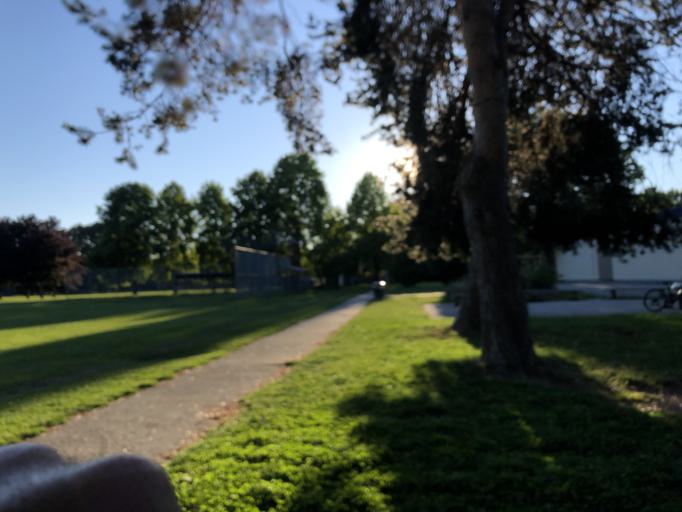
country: CA
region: British Columbia
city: Richmond
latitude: 49.1392
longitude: -123.1199
